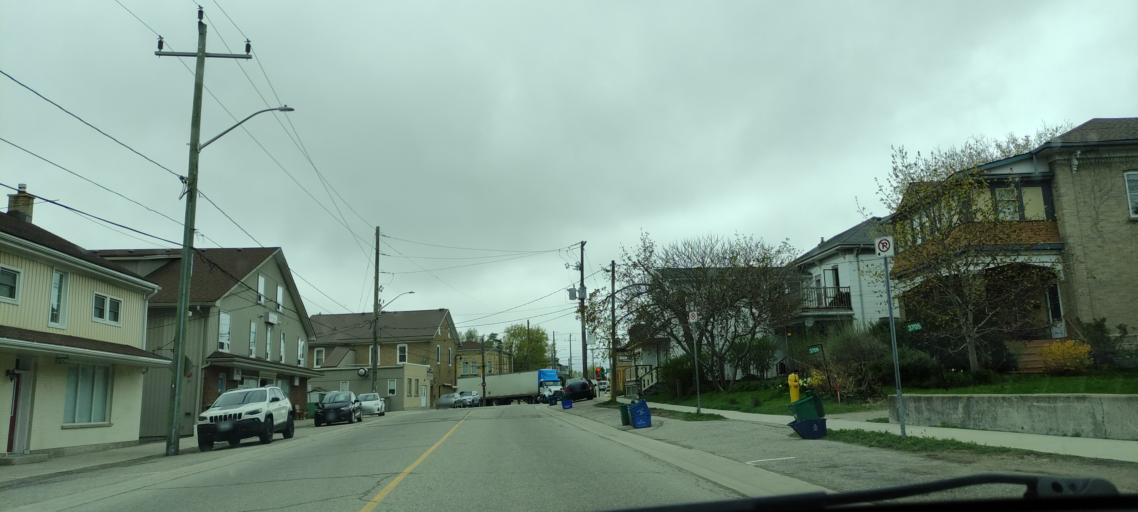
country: CA
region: Ontario
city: Stratford
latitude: 43.4765
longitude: -80.7645
